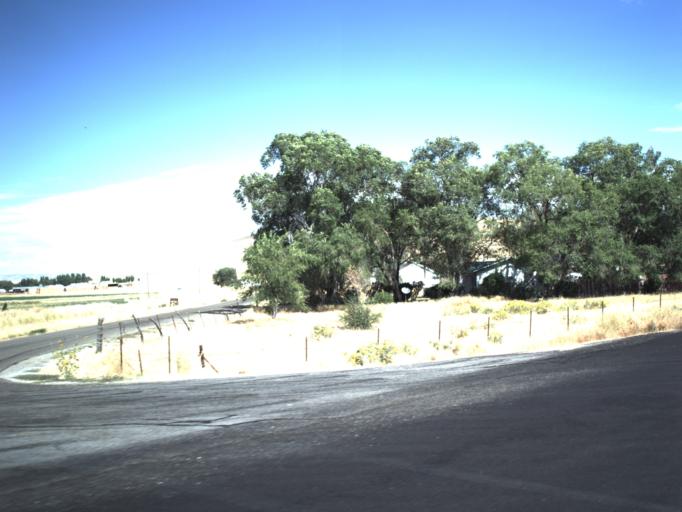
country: US
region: Utah
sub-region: Box Elder County
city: Garland
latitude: 41.7833
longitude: -112.4345
